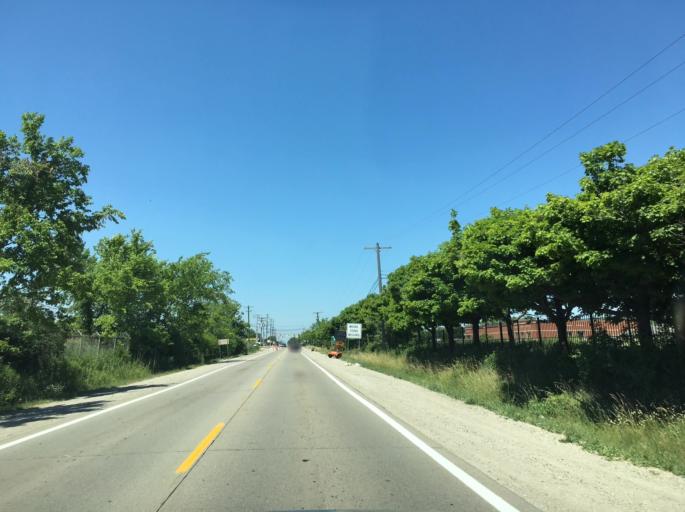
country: US
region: Michigan
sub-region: Macomb County
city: Fraser
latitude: 42.5398
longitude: -82.9051
